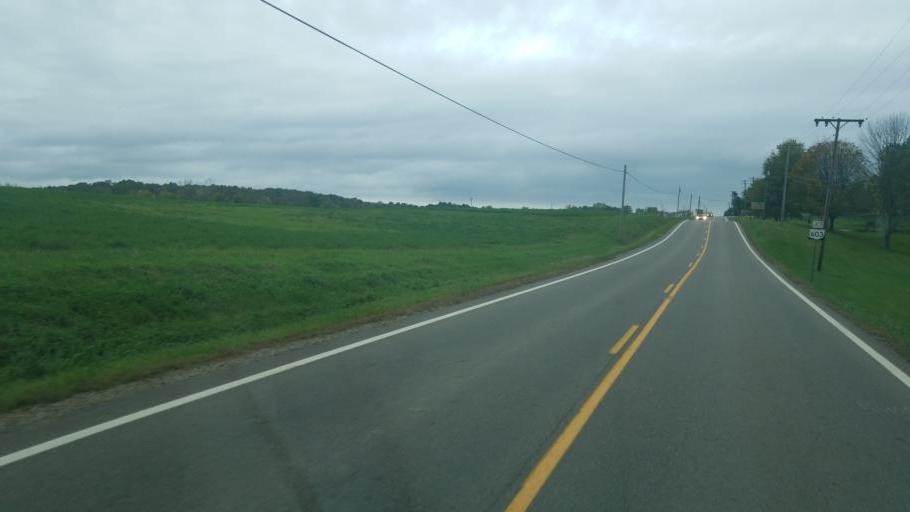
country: US
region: Ohio
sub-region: Richland County
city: Lincoln Heights
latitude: 40.7123
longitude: -82.3752
